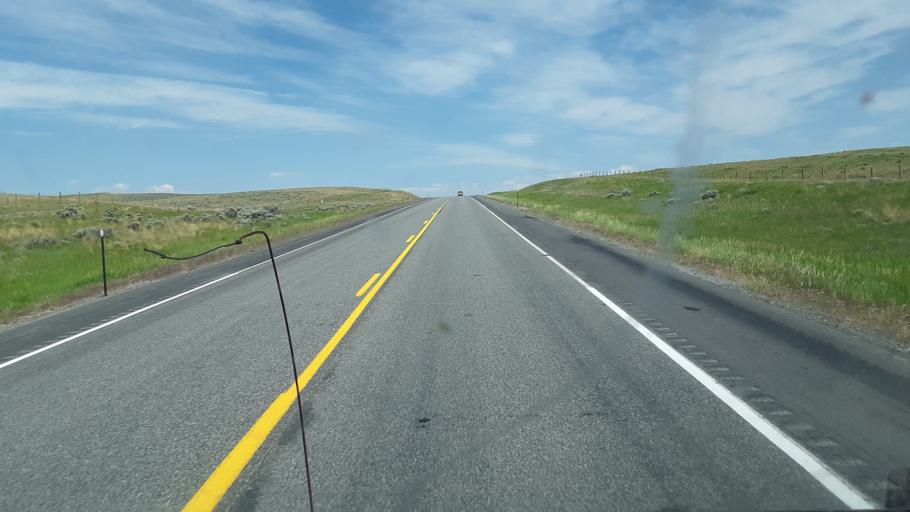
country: US
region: Wyoming
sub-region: Park County
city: Cody
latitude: 44.2839
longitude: -108.8966
